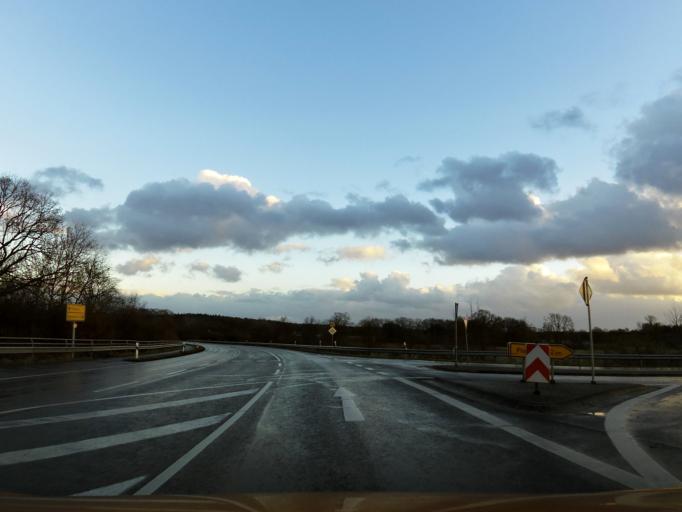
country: DE
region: Lower Saxony
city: Meinersen
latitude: 52.4464
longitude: 10.3117
